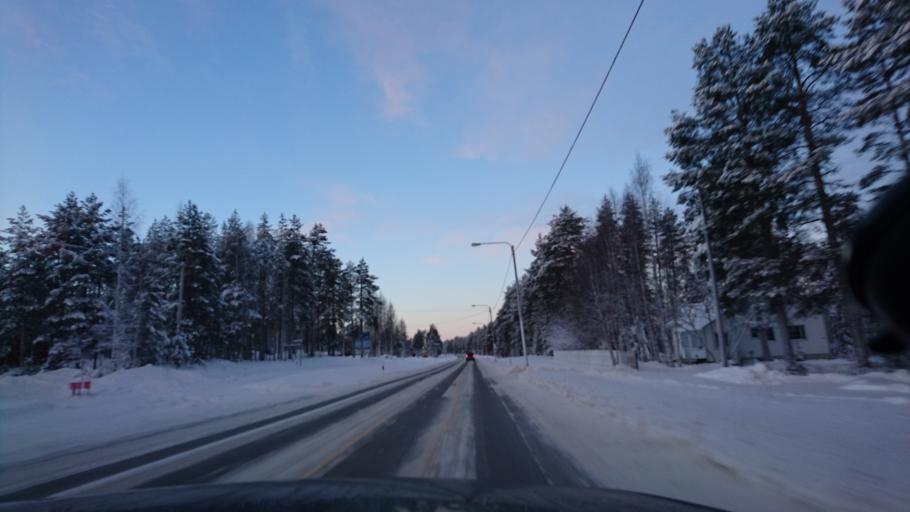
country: FI
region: Lapland
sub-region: Rovaniemi
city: Ranua
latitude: 65.9417
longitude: 26.4767
